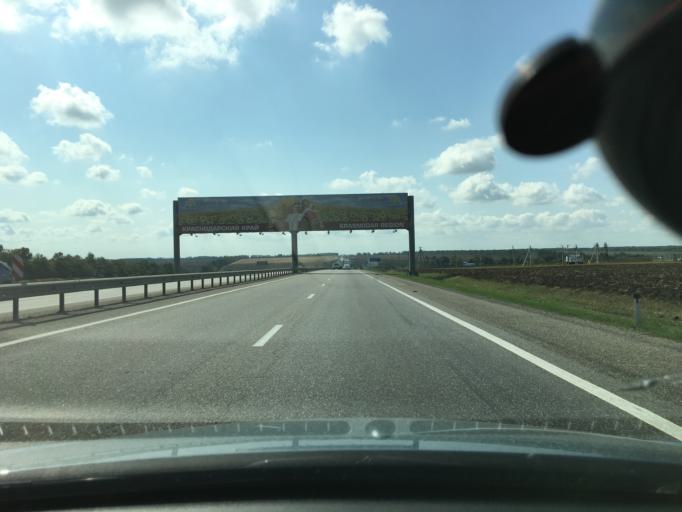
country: RU
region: Krasnodarskiy
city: Krasnoye
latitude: 46.7776
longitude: 39.6642
